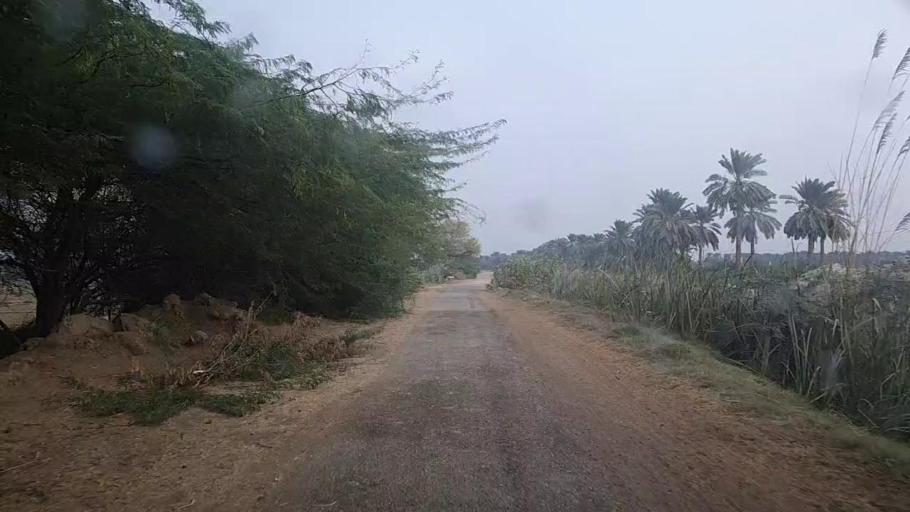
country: PK
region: Sindh
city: Gambat
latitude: 27.3870
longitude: 68.5905
